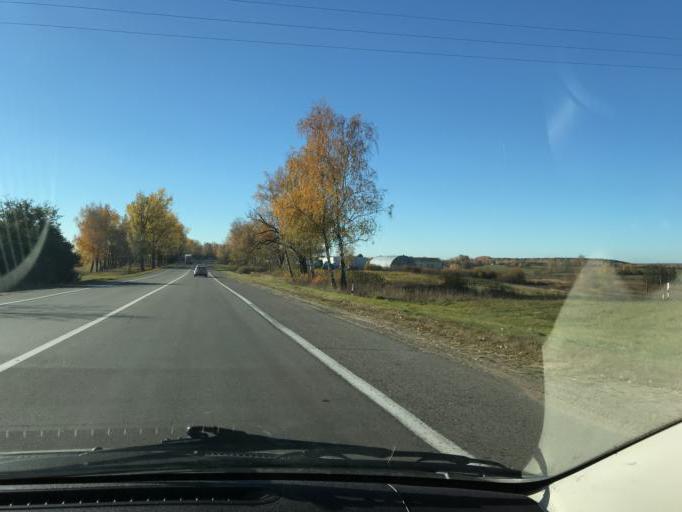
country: BY
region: Vitebsk
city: Lyepyel'
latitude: 54.9309
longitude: 28.7573
